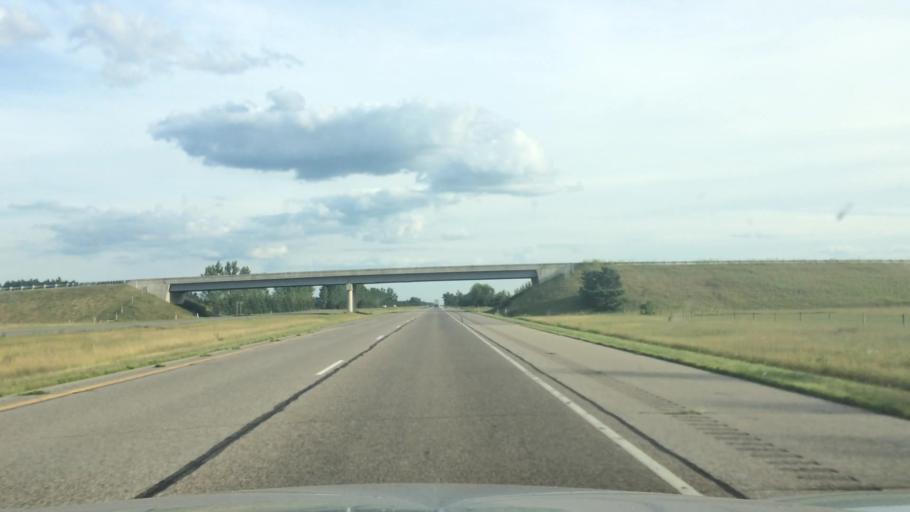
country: US
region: Wisconsin
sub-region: Portage County
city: Plover
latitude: 44.2893
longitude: -89.5237
